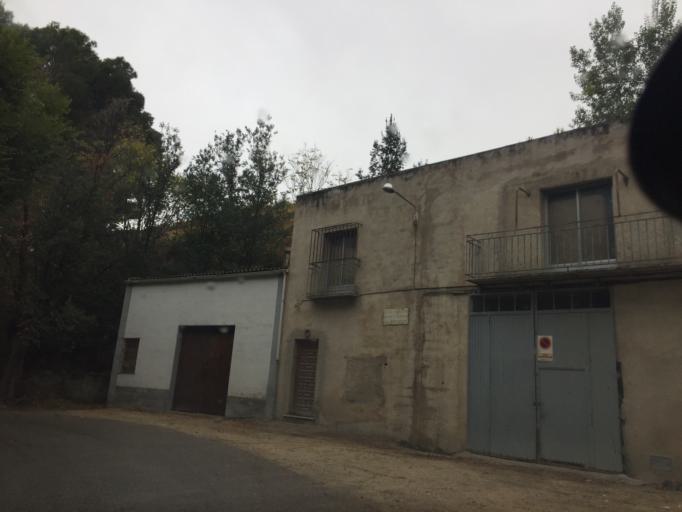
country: ES
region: Andalusia
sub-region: Provincia de Jaen
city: Jimena
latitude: 37.8390
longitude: -3.4718
